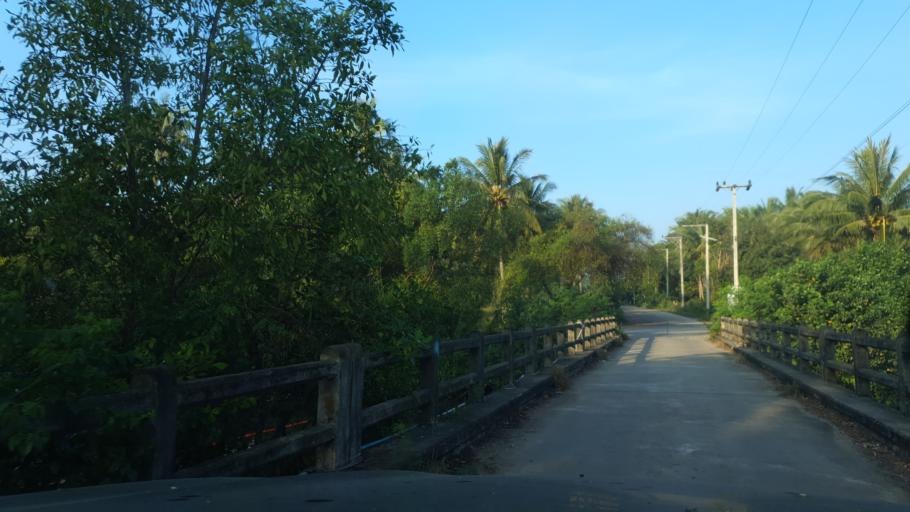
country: TH
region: Prachuap Khiri Khan
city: Bang Saphan
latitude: 11.3049
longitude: 99.5508
